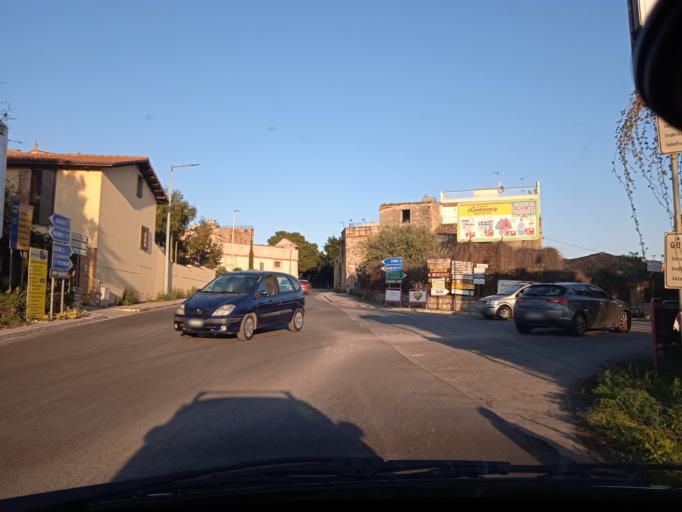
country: IT
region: Sicily
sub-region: Palermo
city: Bagheria
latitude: 38.0894
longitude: 13.5003
